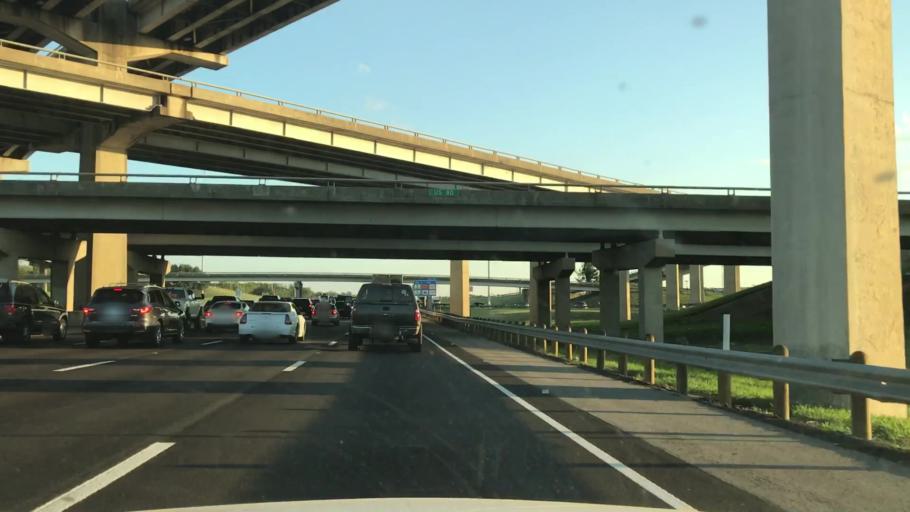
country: US
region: Texas
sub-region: Dallas County
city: Mesquite
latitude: 32.7930
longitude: -96.6254
